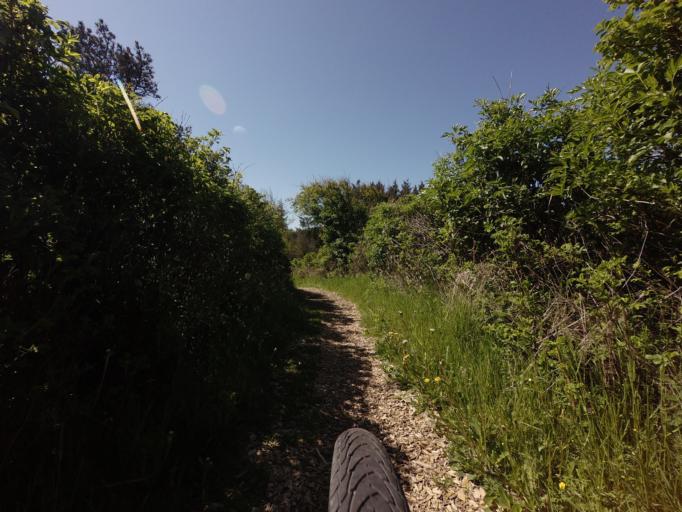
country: DK
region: North Denmark
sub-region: Jammerbugt Kommune
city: Pandrup
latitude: 57.3000
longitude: 9.6516
